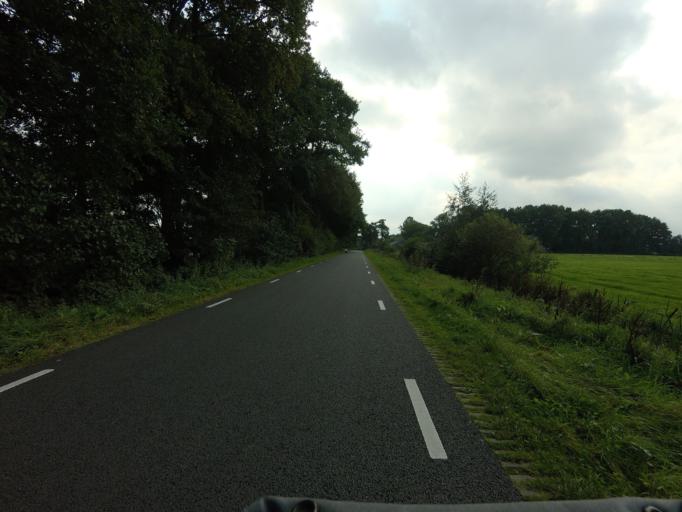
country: NL
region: Utrecht
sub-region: Gemeente Amersfoort
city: Hoogland
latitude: 52.1666
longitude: 5.3459
